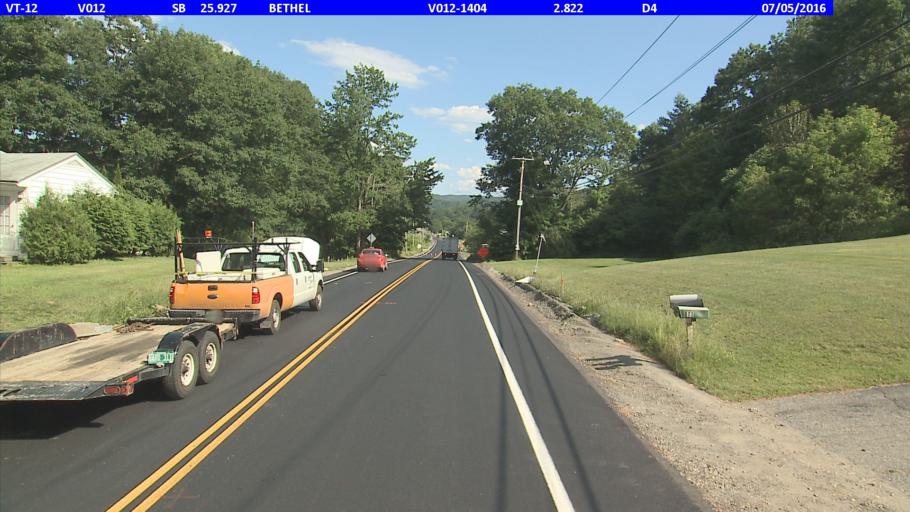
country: US
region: Vermont
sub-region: Orange County
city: Randolph
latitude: 43.8390
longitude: -72.6488
